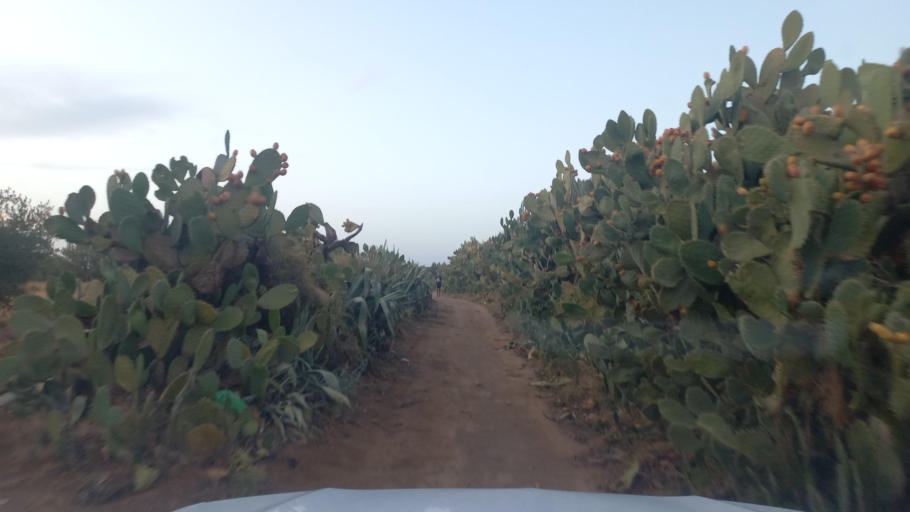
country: TN
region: Al Qasrayn
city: Kasserine
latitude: 35.2234
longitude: 9.0510
